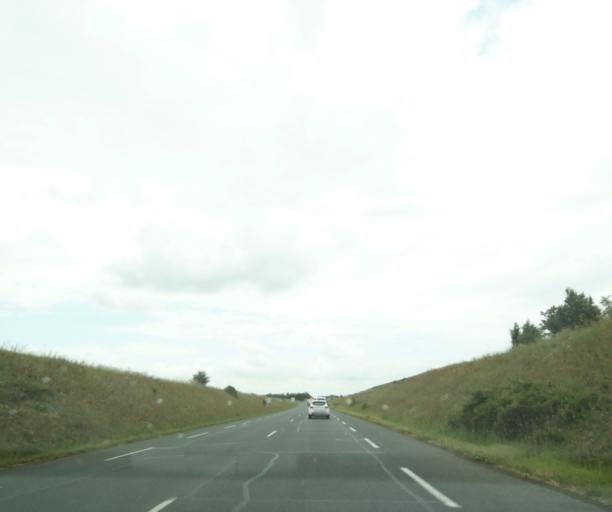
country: FR
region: Poitou-Charentes
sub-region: Departement des Deux-Sevres
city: Louzy
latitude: 47.0036
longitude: -0.1942
